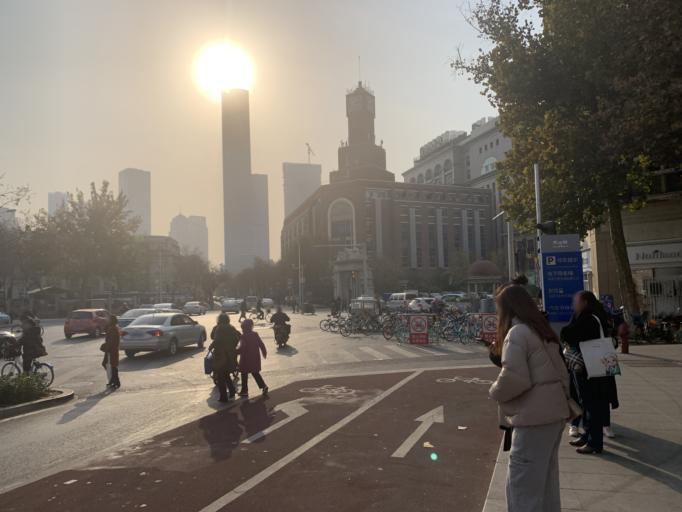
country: CN
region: Tianjin Shi
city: Quanyechang
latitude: 39.1255
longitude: 117.1977
